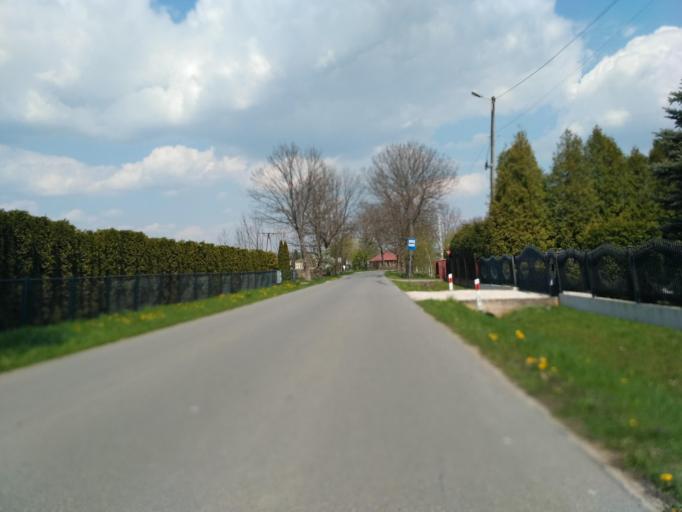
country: PL
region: Subcarpathian Voivodeship
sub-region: Powiat jasielski
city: Tarnowiec
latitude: 49.7398
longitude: 21.5438
